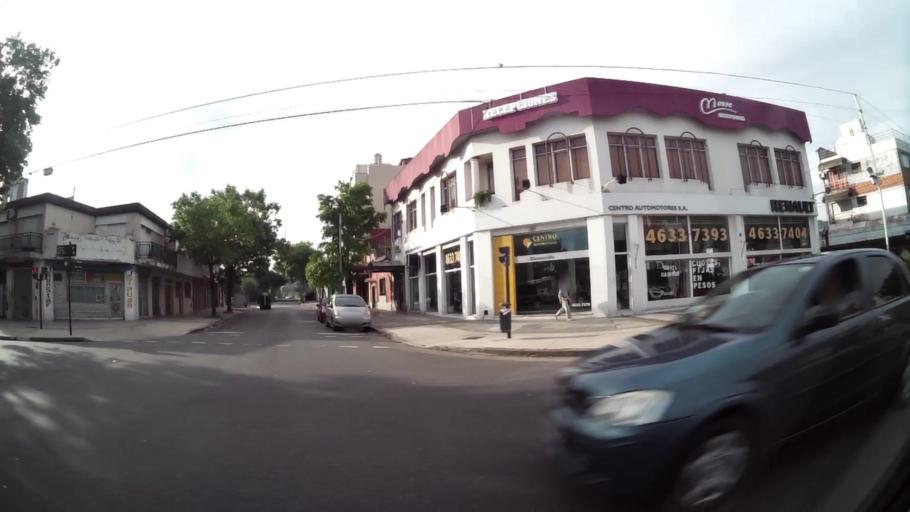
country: AR
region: Buenos Aires F.D.
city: Villa Santa Rita
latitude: -34.6417
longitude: -58.4580
